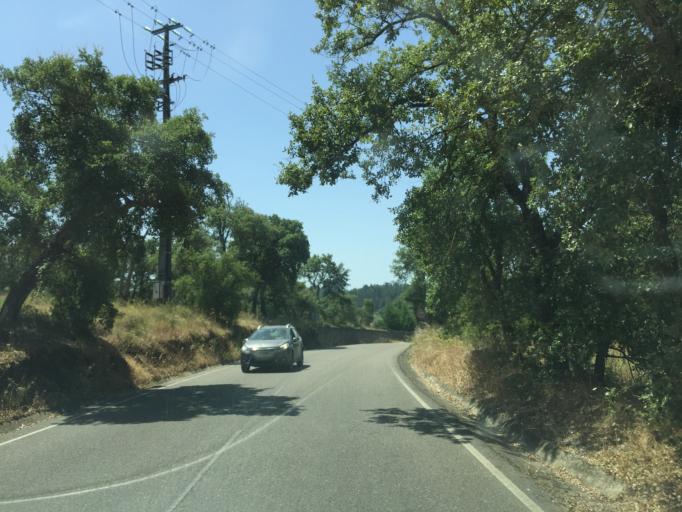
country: PT
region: Santarem
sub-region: Ferreira do Zezere
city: Ferreira do Zezere
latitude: 39.6206
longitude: -8.3107
